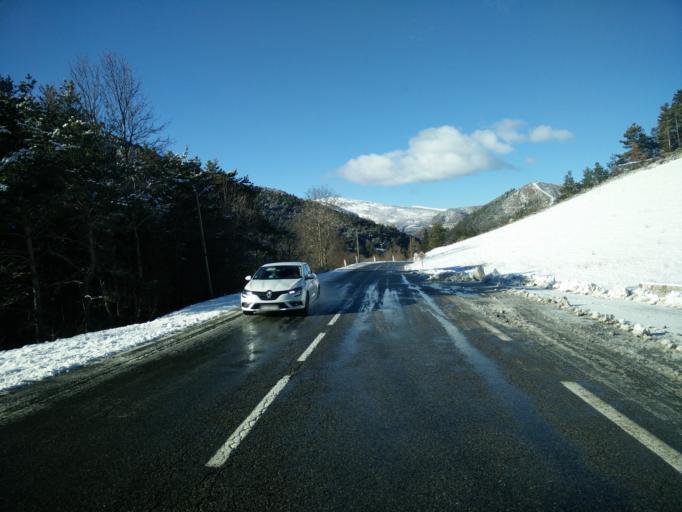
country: FR
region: Provence-Alpes-Cote d'Azur
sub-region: Departement des Alpes-de-Haute-Provence
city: Annot
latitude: 43.9125
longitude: 6.5946
